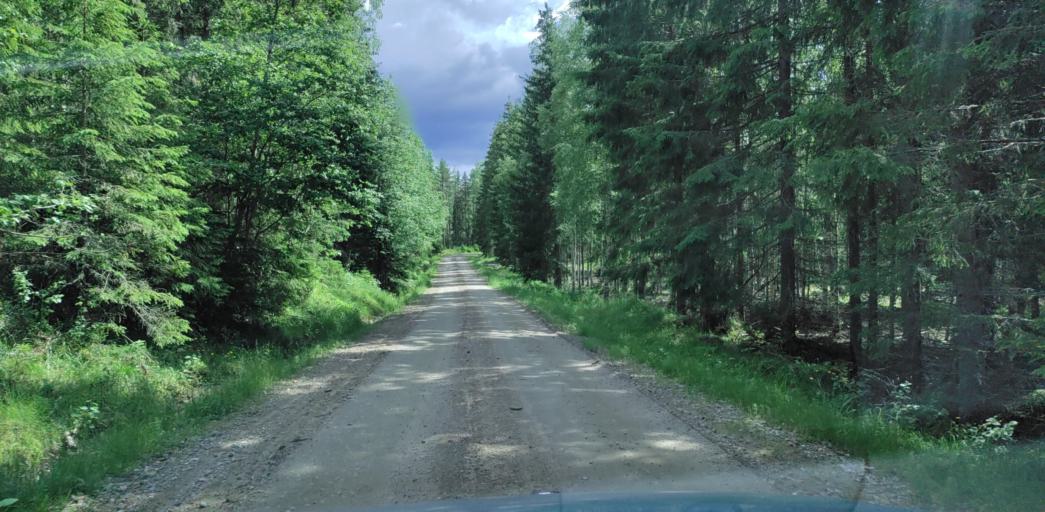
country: SE
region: Vaermland
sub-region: Hagfors Kommun
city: Ekshaerad
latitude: 60.0600
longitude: 13.3096
